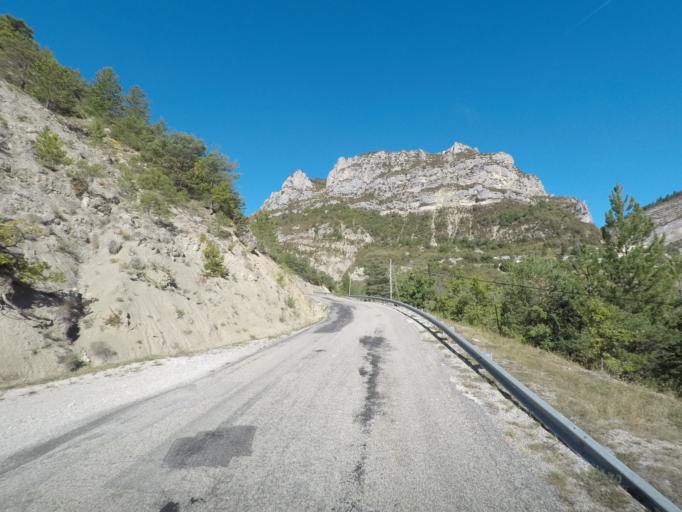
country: FR
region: Rhone-Alpes
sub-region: Departement de la Drome
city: Buis-les-Baronnies
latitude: 44.5051
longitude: 5.3466
